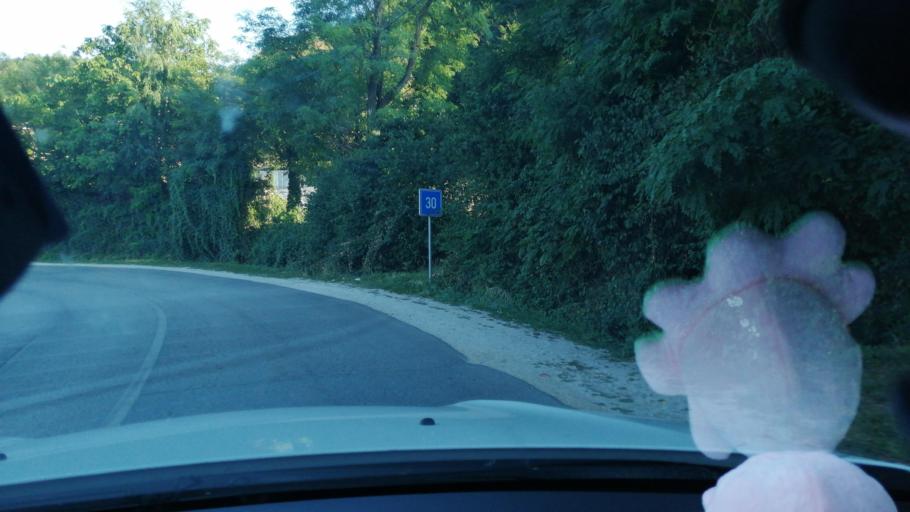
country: RS
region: Central Serbia
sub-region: Moravicki Okrug
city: Cacak
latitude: 43.8423
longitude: 20.2871
